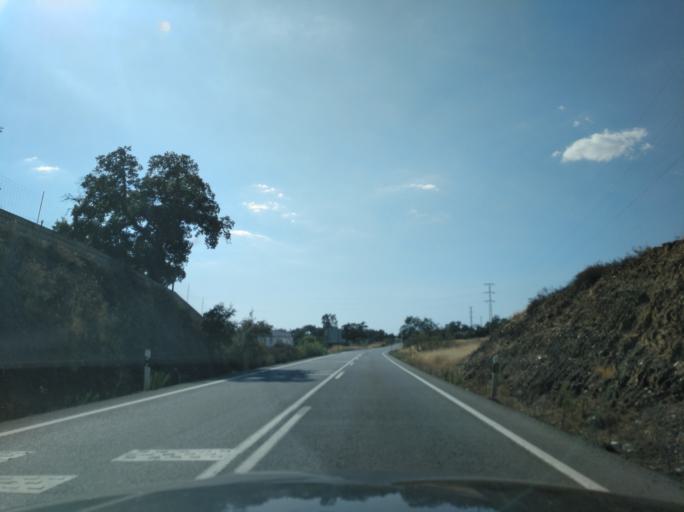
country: ES
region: Andalusia
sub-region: Provincia de Huelva
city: Santa Barbara de Casa
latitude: 37.7924
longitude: -7.1874
